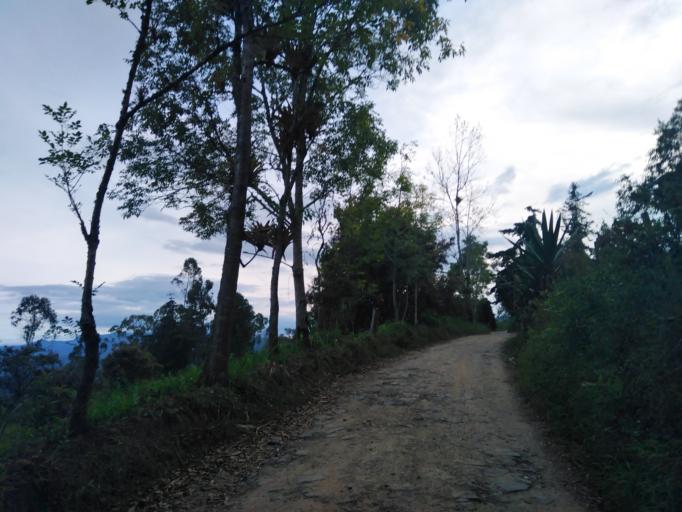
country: CO
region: Cundinamarca
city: Tenza
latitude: 5.0985
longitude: -73.4146
